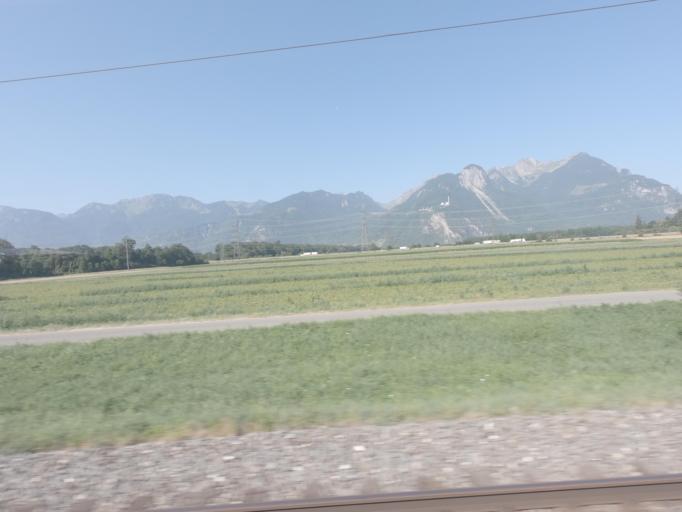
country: CH
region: Valais
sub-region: Monthey District
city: Vouvry
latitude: 46.3525
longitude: 6.9313
